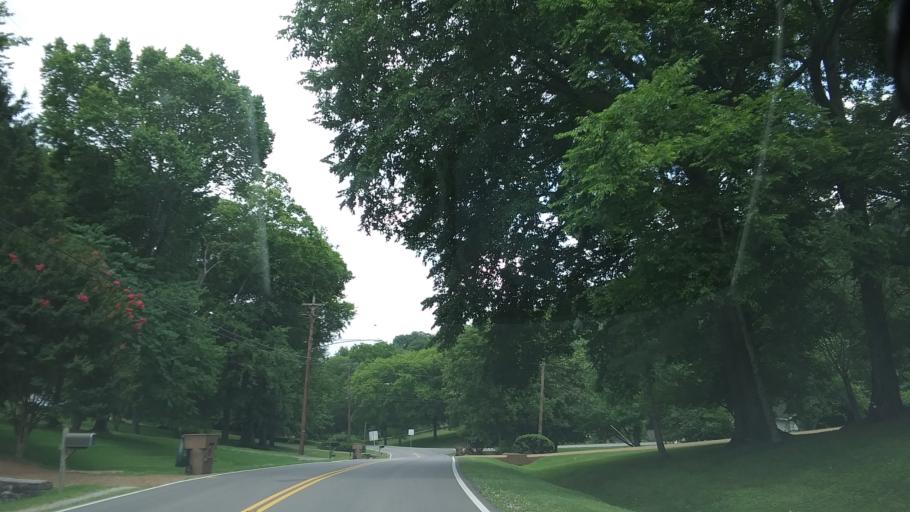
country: US
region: Tennessee
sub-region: Davidson County
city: Belle Meade
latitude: 36.1378
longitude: -86.8707
